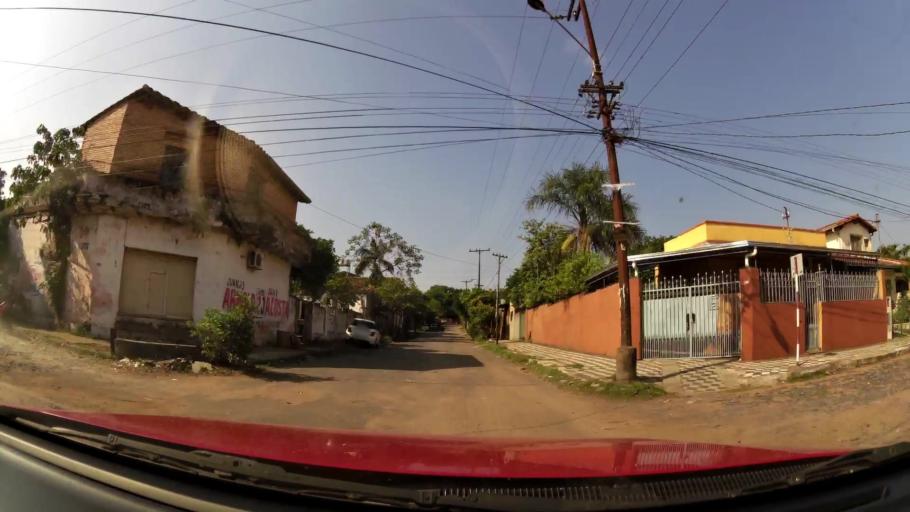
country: PY
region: Asuncion
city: Asuncion
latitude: -25.3132
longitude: -57.6366
